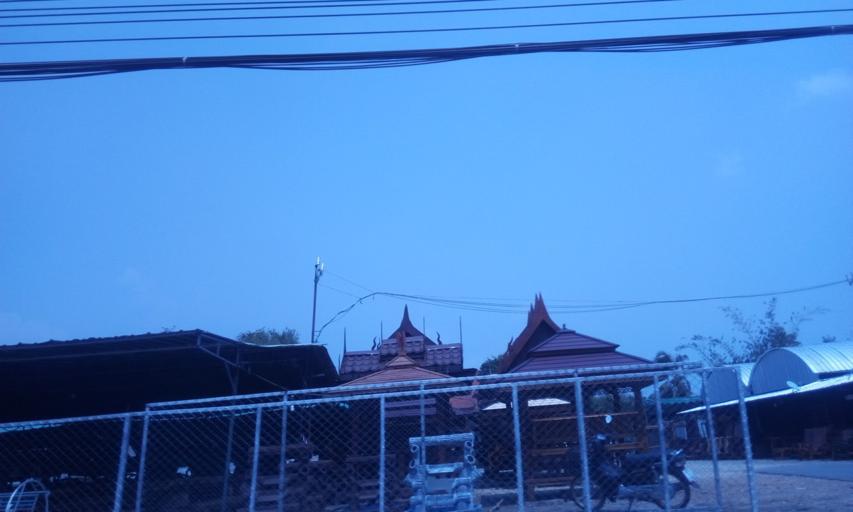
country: TH
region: Chon Buri
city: Phanat Nikhom
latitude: 13.4435
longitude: 101.1777
